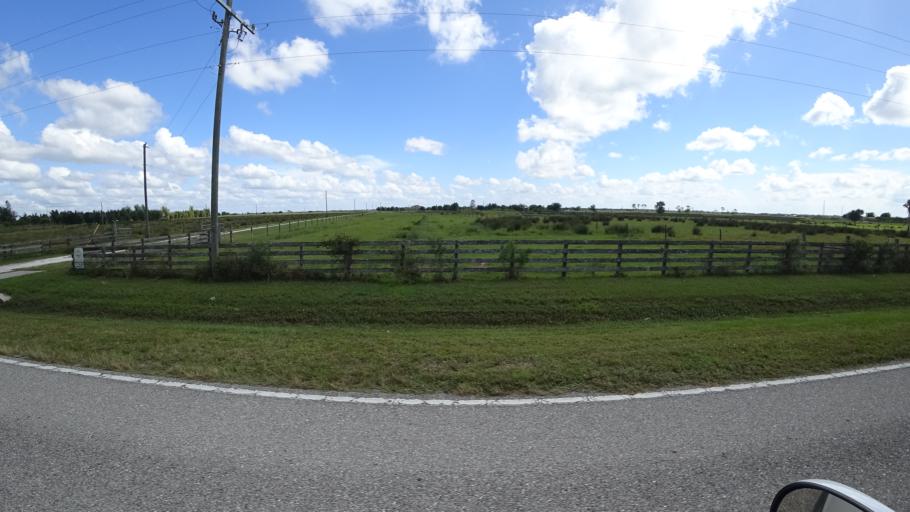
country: US
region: Florida
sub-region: Sarasota County
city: Warm Mineral Springs
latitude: 27.2926
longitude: -82.1908
